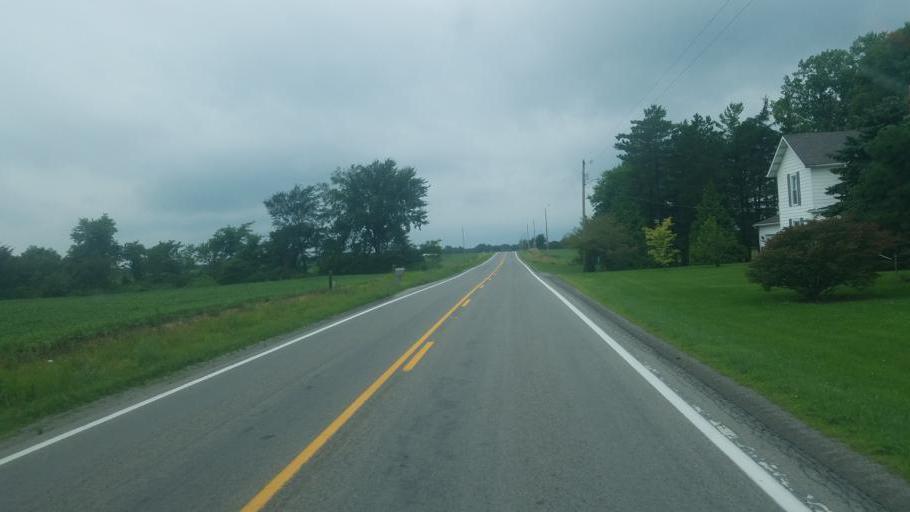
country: US
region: Ohio
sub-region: Logan County
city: Northwood
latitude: 40.5931
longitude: -83.7673
